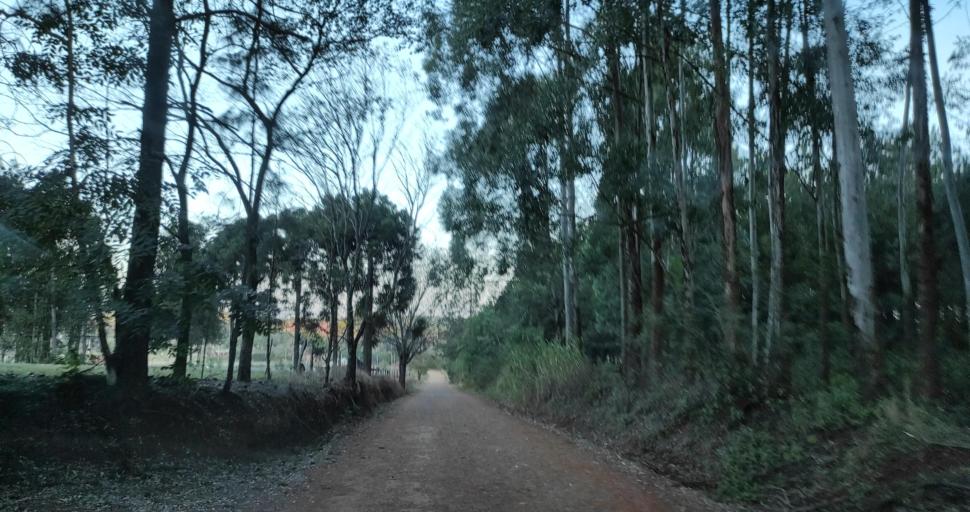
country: AR
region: Misiones
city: Capiovi
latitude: -26.8898
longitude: -55.0767
